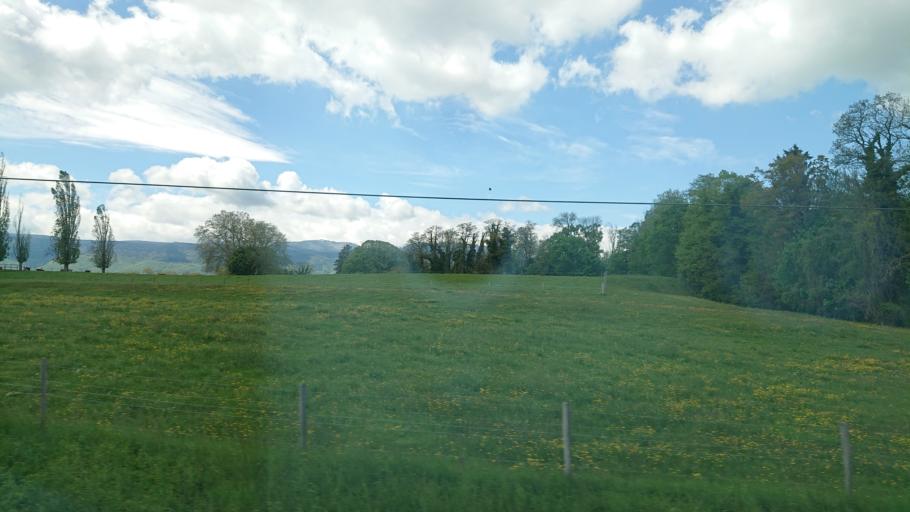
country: CH
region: Vaud
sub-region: Nyon District
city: Nyon
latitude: 46.3774
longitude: 6.2275
